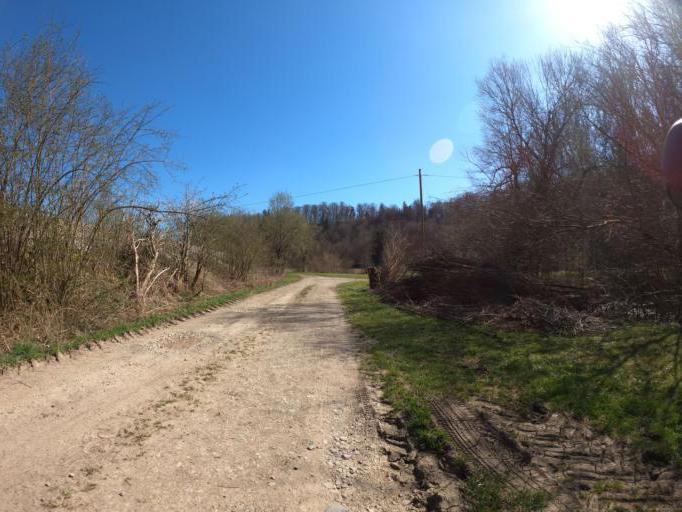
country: DE
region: Baden-Wuerttemberg
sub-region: Tuebingen Region
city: Haigerloch
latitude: 48.3791
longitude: 8.7917
